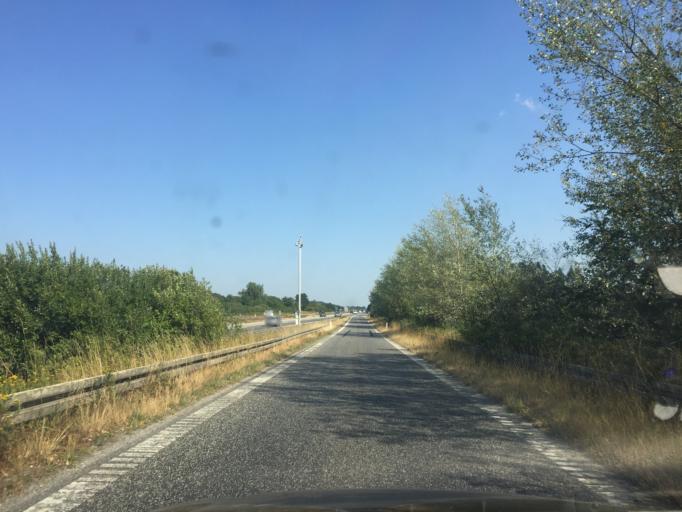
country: DK
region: South Denmark
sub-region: Assens Kommune
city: Vissenbjerg
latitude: 55.4004
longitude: 10.1584
